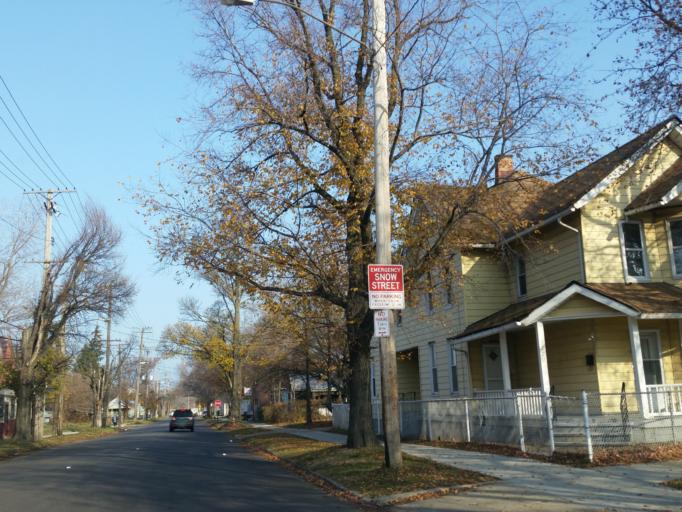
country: US
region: Ohio
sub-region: Cuyahoga County
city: Brooklyn
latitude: 41.4741
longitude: -81.7348
